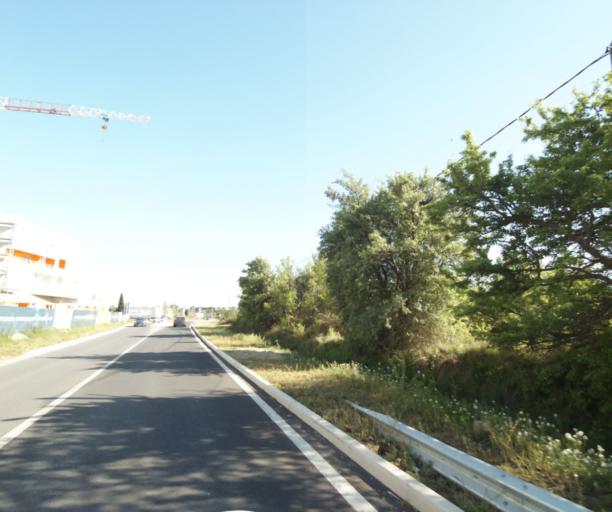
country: FR
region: Languedoc-Roussillon
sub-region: Departement de l'Herault
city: Perols
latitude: 43.5753
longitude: 3.9350
